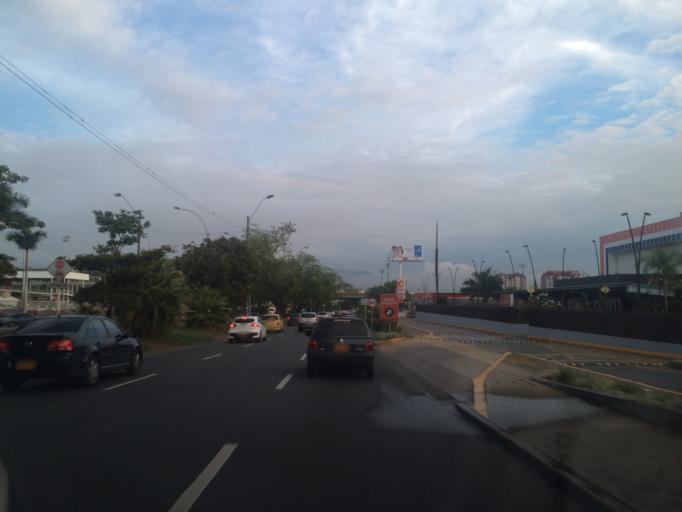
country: CO
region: Valle del Cauca
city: Cali
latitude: 3.3843
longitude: -76.5383
